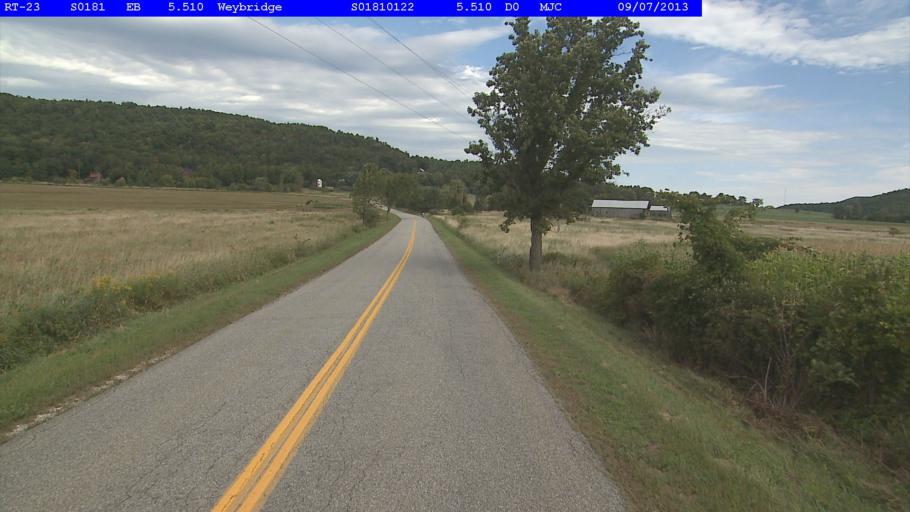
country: US
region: Vermont
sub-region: Addison County
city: Vergennes
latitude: 44.0703
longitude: -73.2505
